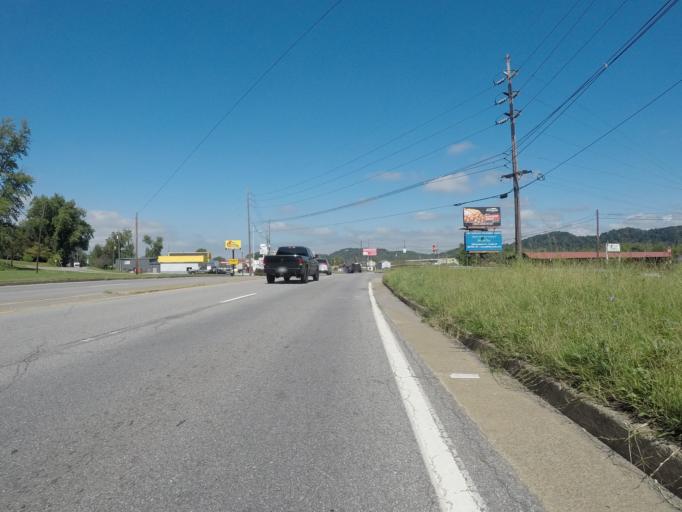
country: US
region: Kentucky
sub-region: Boyd County
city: Ashland
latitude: 38.4640
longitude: -82.6166
